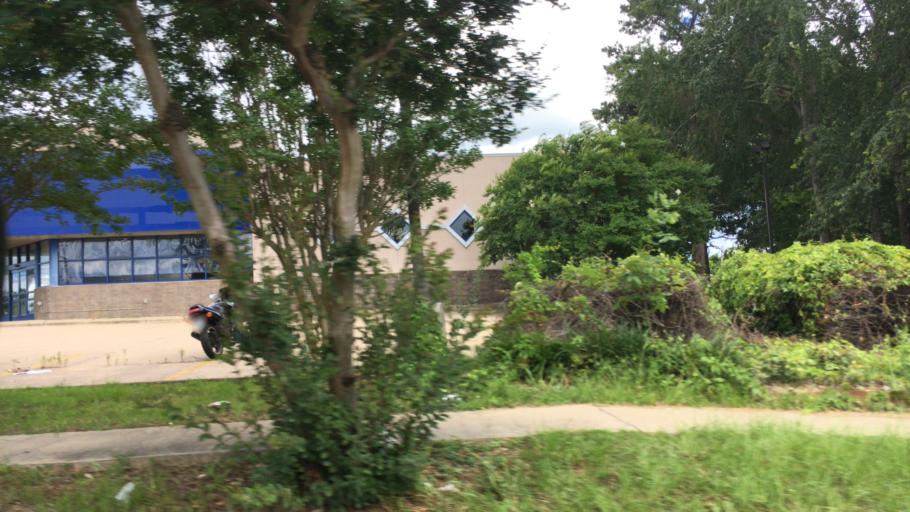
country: US
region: Louisiana
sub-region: Lincoln Parish
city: Ruston
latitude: 32.5234
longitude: -92.6396
